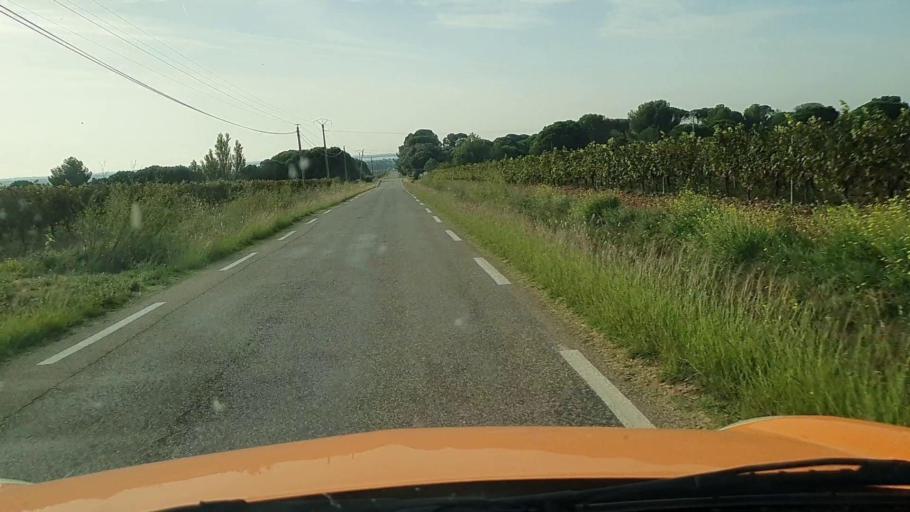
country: FR
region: Languedoc-Roussillon
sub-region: Departement du Gard
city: Beauvoisin
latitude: 43.6615
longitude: 4.3433
